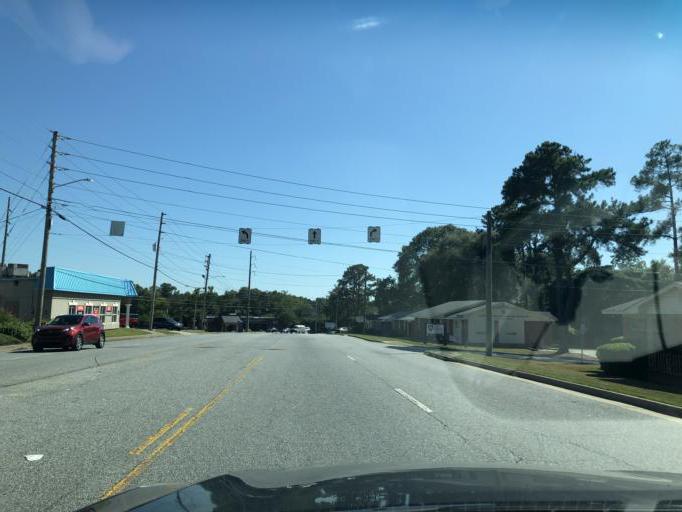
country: US
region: Georgia
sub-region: Muscogee County
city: Columbus
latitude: 32.5037
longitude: -84.9529
